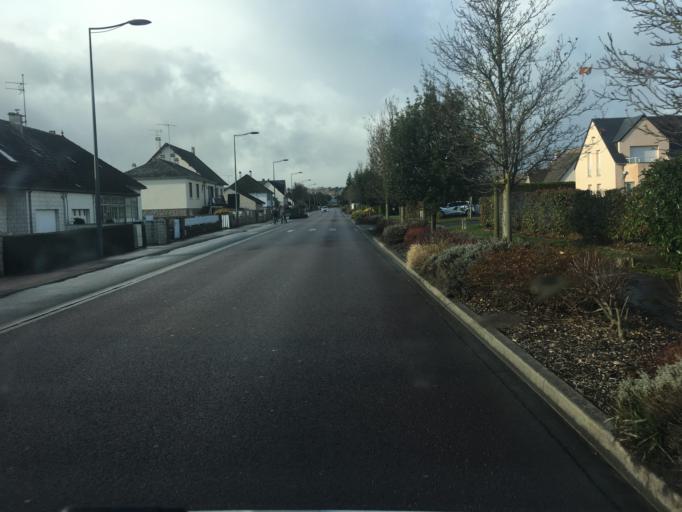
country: FR
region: Lower Normandy
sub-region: Departement de la Manche
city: Quettehou
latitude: 49.5907
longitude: -1.2912
